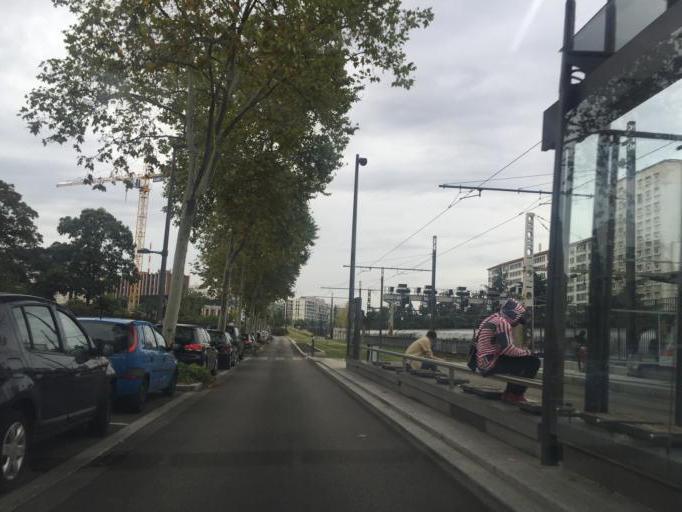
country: FR
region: Rhone-Alpes
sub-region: Departement du Rhone
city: Lyon
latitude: 45.7457
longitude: 4.8591
